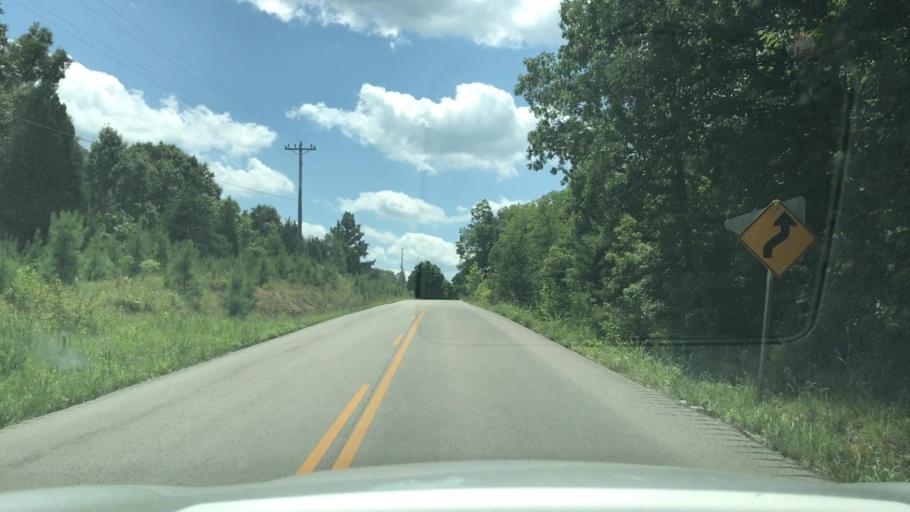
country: US
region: Kentucky
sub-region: Hopkins County
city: Nortonville
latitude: 37.1179
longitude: -87.3238
